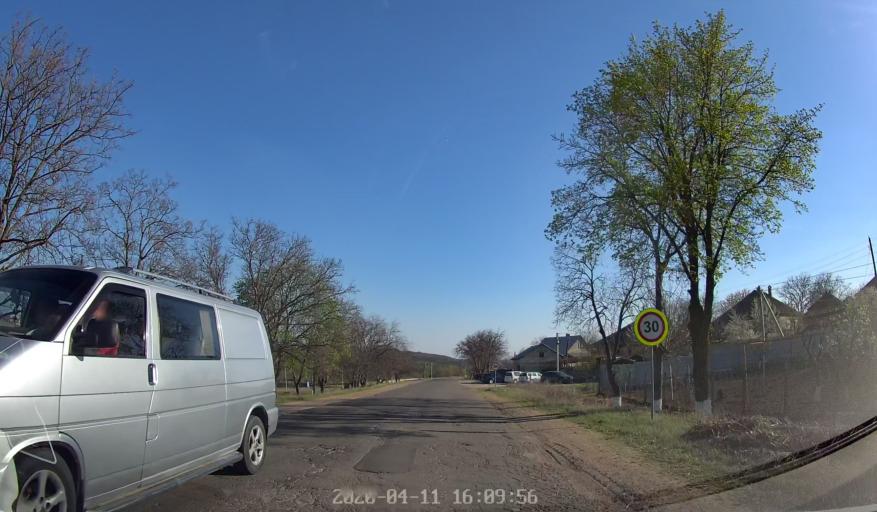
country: MD
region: Chisinau
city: Vadul lui Voda
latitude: 47.0708
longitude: 29.1362
